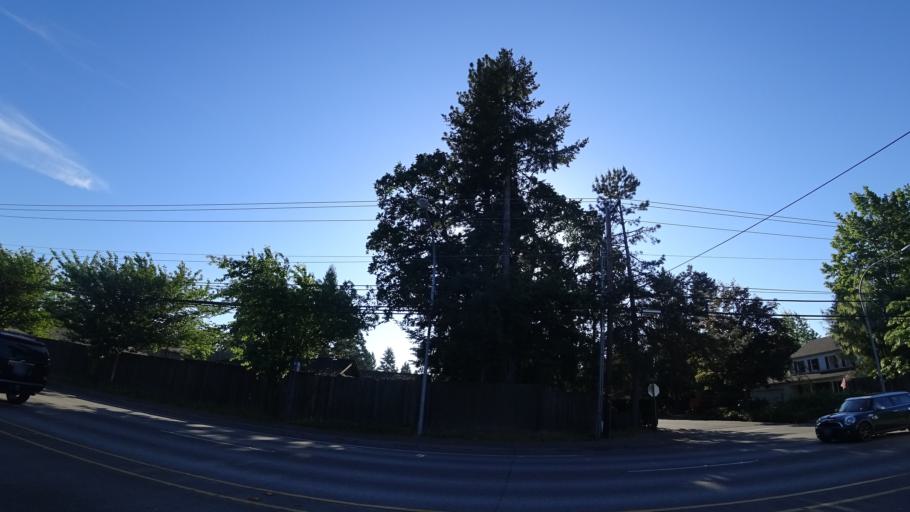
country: US
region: Oregon
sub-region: Washington County
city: Aloha
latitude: 45.5111
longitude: -122.8674
